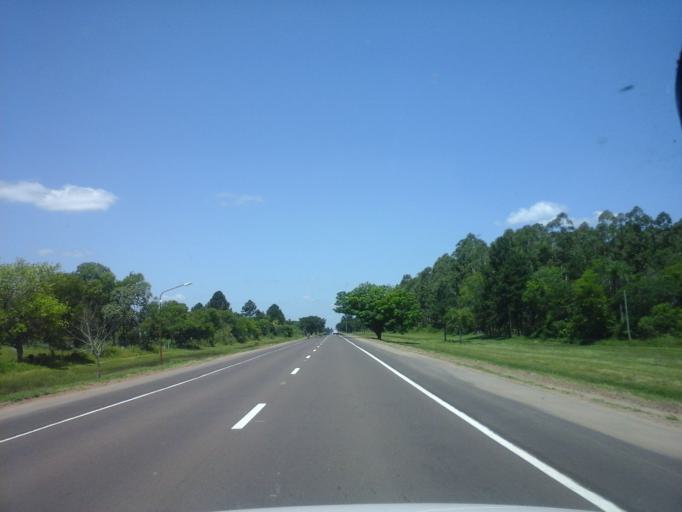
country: AR
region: Corrientes
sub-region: Departamento de San Cosme
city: San Cosme
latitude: -27.3675
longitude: -58.3750
